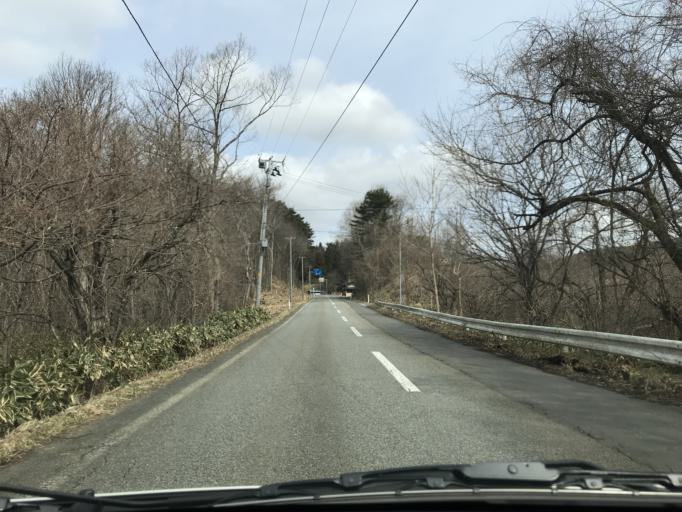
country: JP
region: Iwate
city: Kitakami
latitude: 39.2555
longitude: 141.3167
